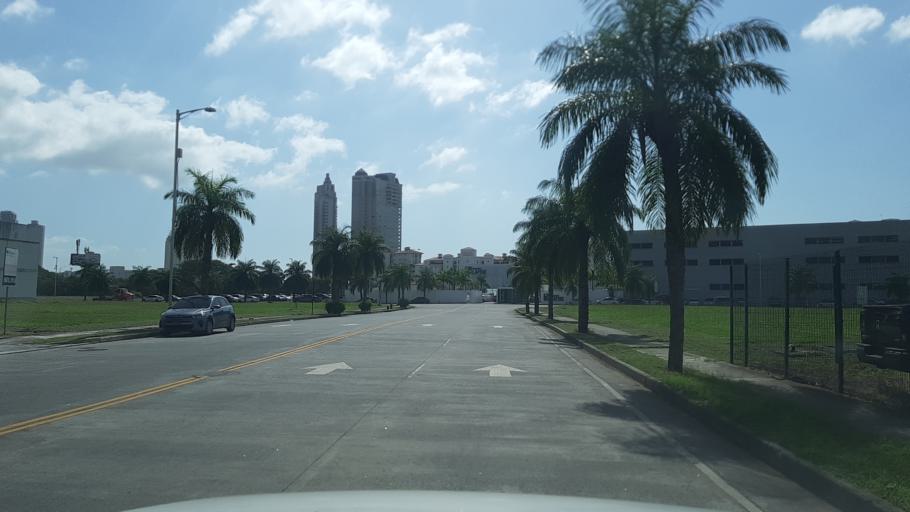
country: PA
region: Panama
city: San Miguelito
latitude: 9.0307
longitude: -79.4590
